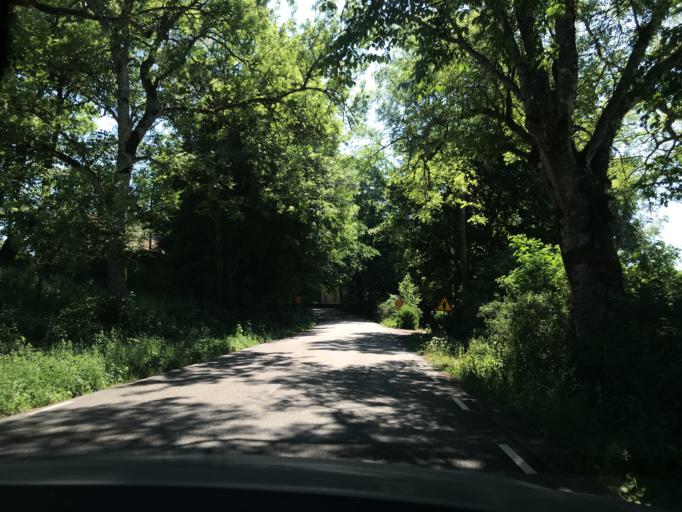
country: SE
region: Vaestra Goetaland
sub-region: Gotene Kommun
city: Kallby
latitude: 58.5795
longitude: 13.3722
